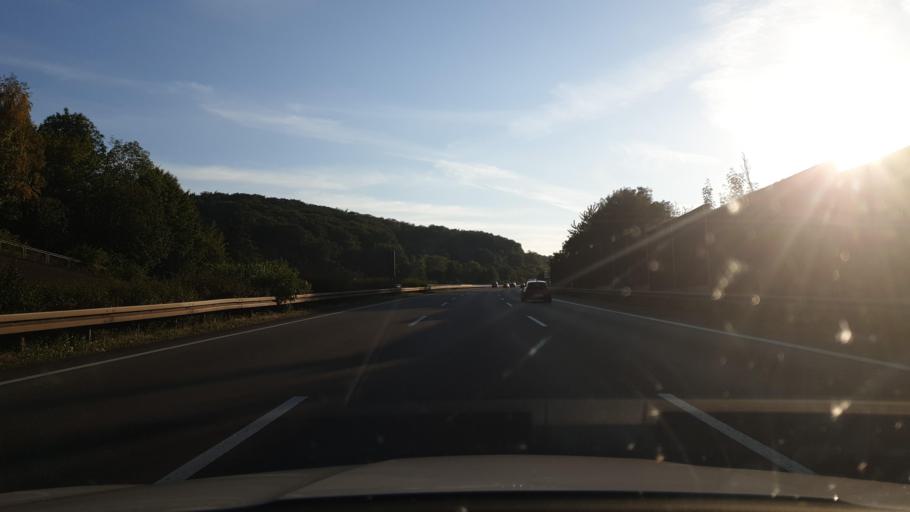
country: DE
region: Lower Saxony
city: Luhden
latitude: 52.2209
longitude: 9.0939
